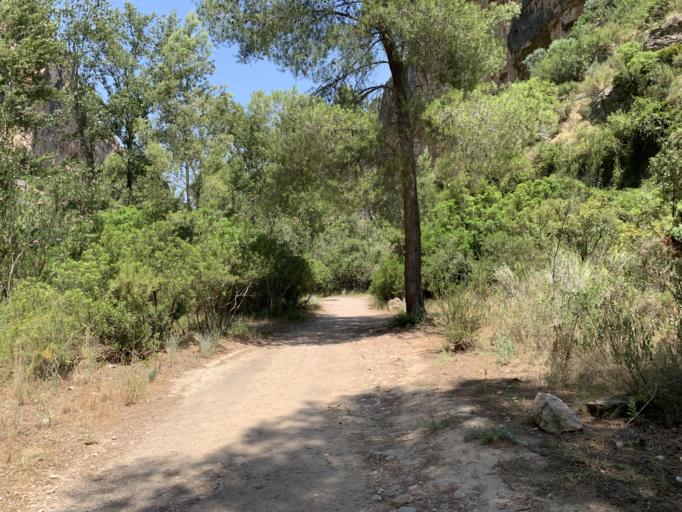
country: ES
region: Valencia
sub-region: Provincia de Valencia
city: Chulilla
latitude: 39.6620
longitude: -0.8937
